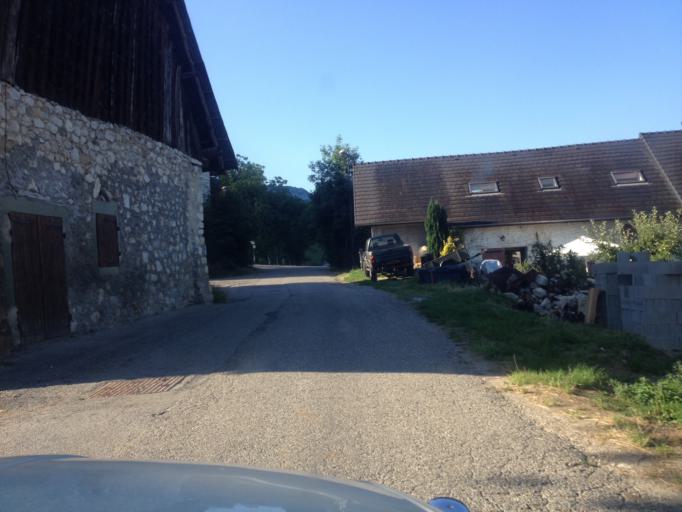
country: FR
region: Rhone-Alpes
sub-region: Departement de la Savoie
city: Mouxy
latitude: 45.6708
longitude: 5.9417
